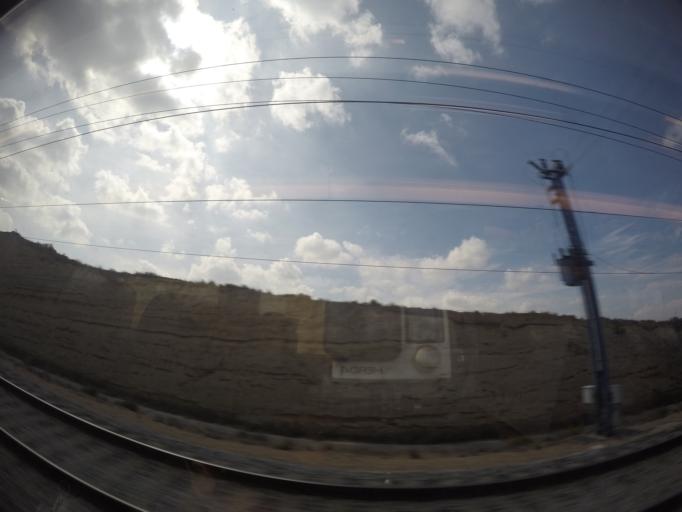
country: ES
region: Aragon
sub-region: Provincia de Zaragoza
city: El Burgo de Ebro
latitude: 41.5573
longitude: -0.7652
